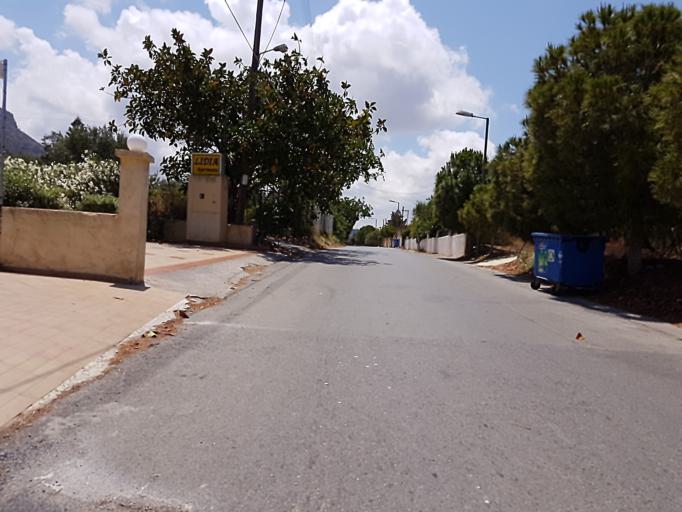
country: GR
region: Crete
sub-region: Nomos Irakleiou
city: Limin Khersonisou
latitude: 35.3152
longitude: 25.3810
